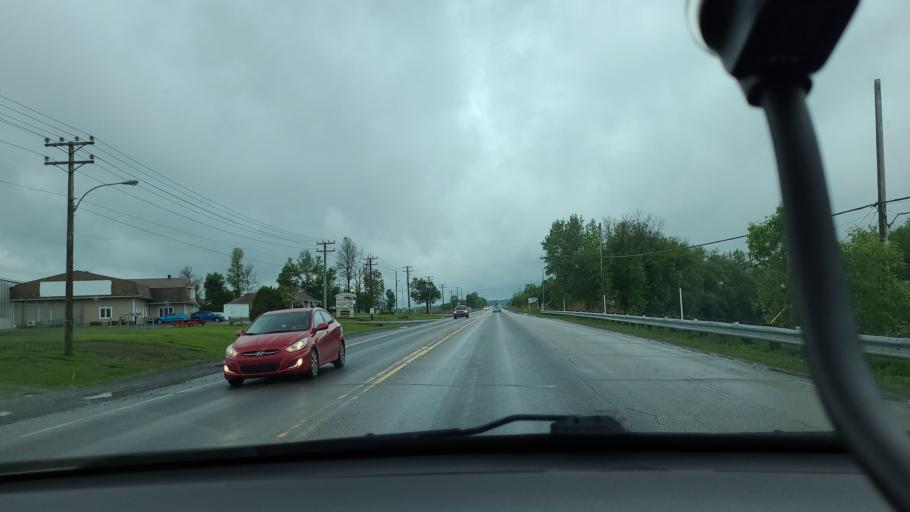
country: CA
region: Quebec
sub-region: Laurentides
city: Saint-Jerome
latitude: 45.7341
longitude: -74.0460
